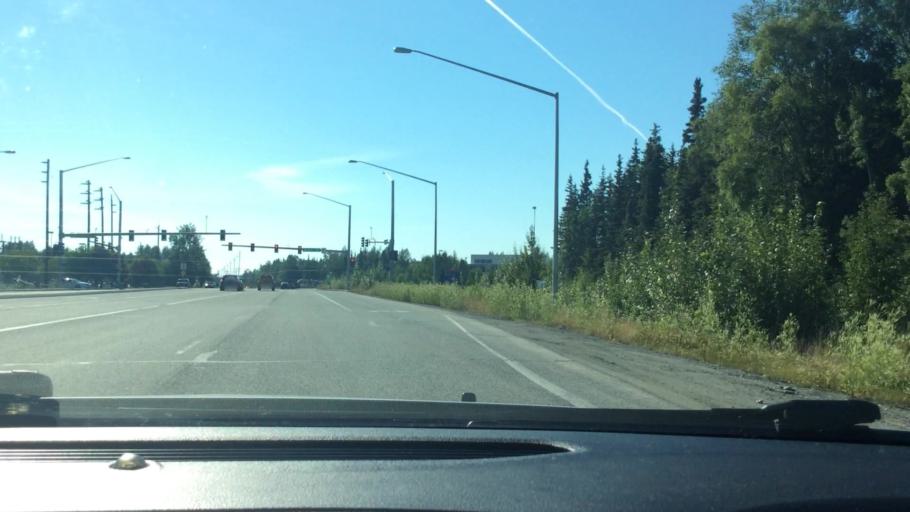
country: US
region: Alaska
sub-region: Anchorage Municipality
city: Elmendorf Air Force Base
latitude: 61.2311
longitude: -149.7389
